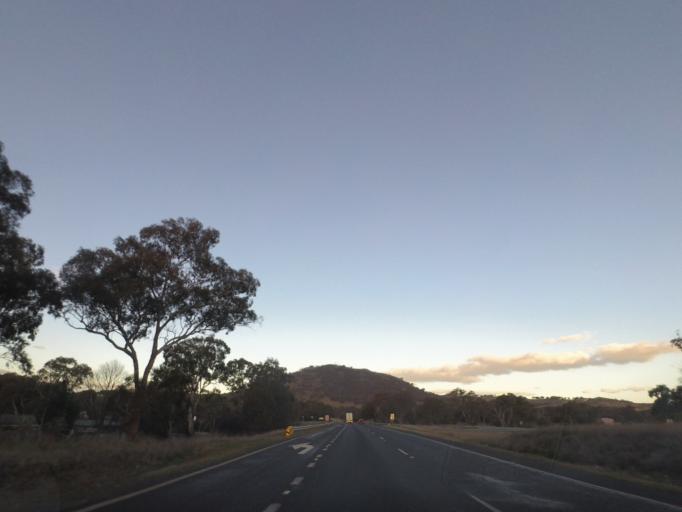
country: AU
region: New South Wales
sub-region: Yass Valley
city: Yass
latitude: -34.7715
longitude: 148.8087
